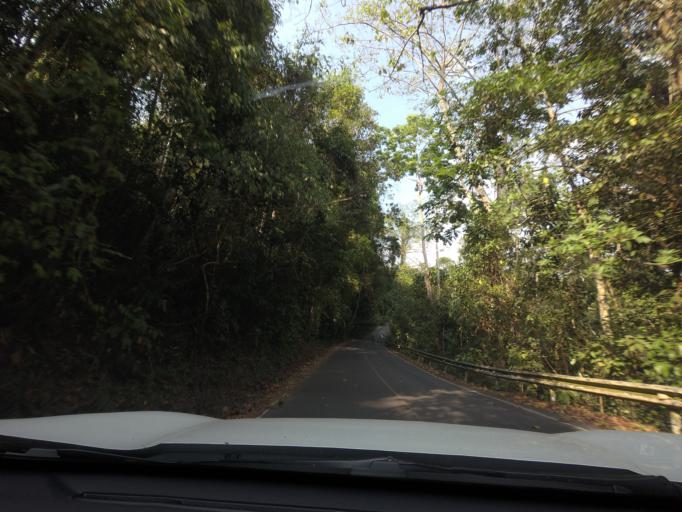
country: TH
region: Nakhon Ratchasima
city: Pak Chong
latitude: 14.4345
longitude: 101.4055
